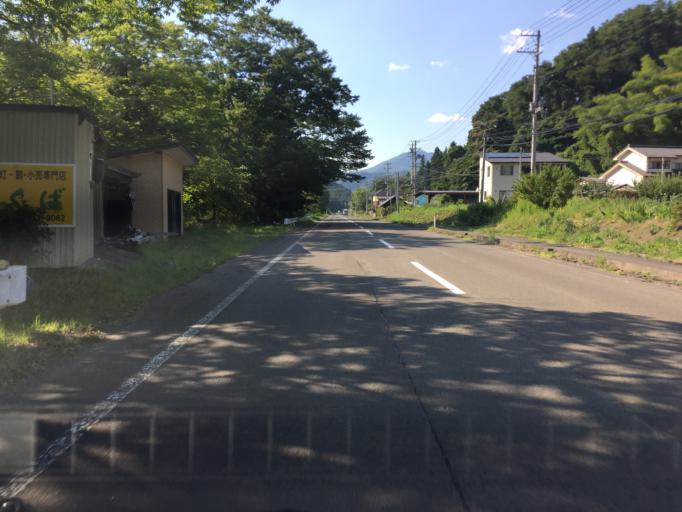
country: JP
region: Fukushima
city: Hobaramachi
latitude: 37.9058
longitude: 140.4297
